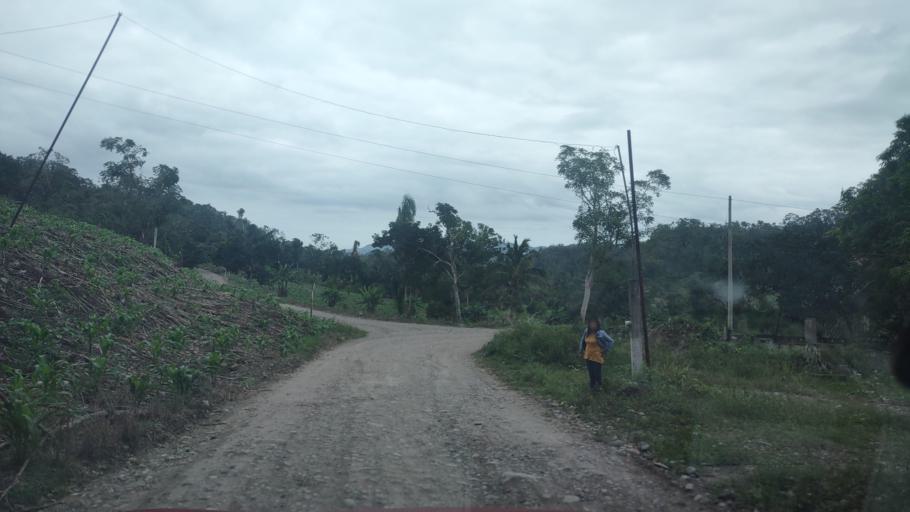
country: MX
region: Veracruz
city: Papantla de Olarte
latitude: 20.4227
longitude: -97.2675
